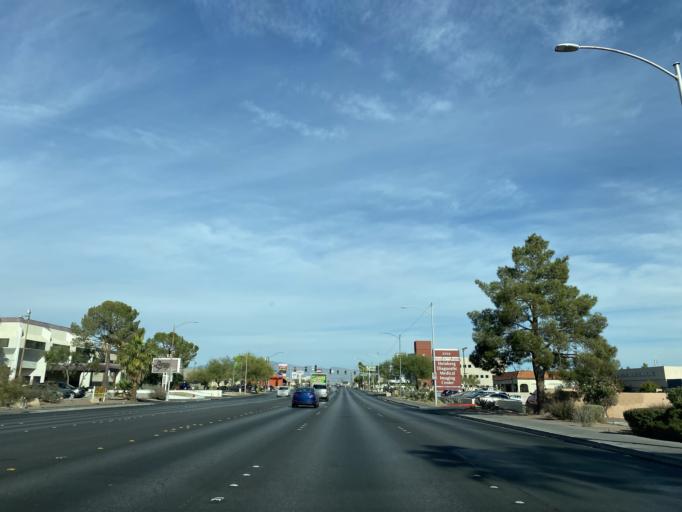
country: US
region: Nevada
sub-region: Clark County
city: Winchester
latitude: 36.1354
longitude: -115.1368
